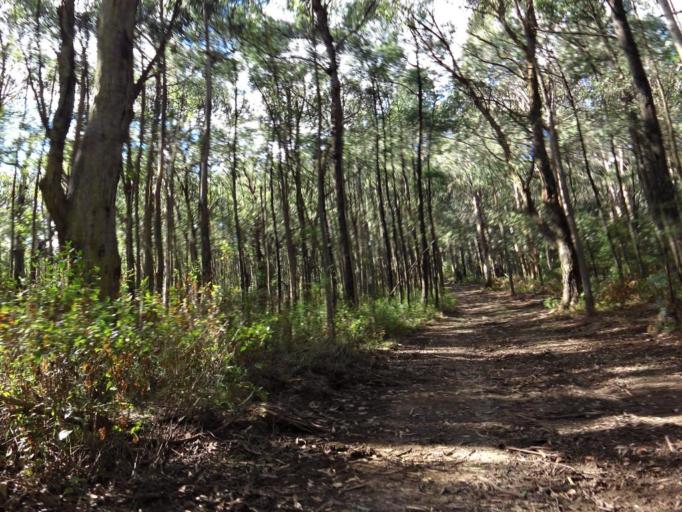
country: AU
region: Victoria
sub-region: Yarra Ranges
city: Millgrove
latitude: -37.7659
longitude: 145.6663
